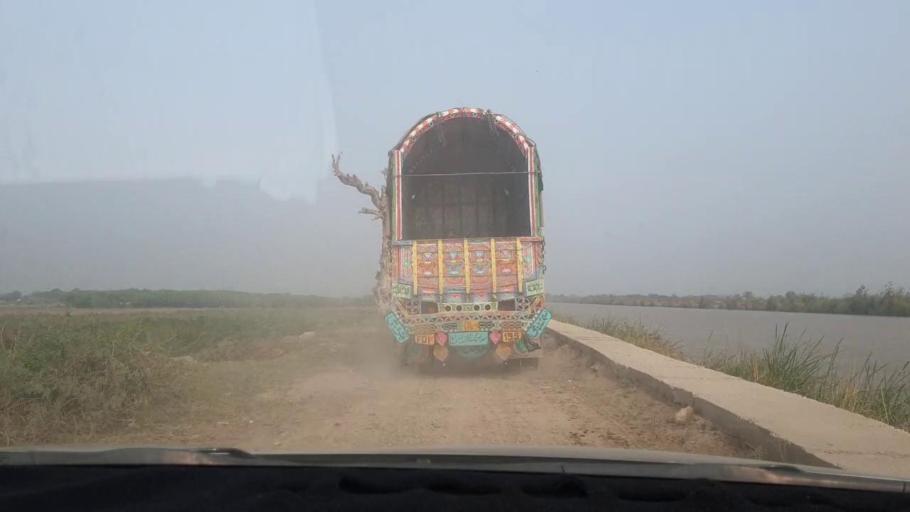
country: PK
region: Sindh
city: Matiari
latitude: 25.6539
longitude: 68.5613
